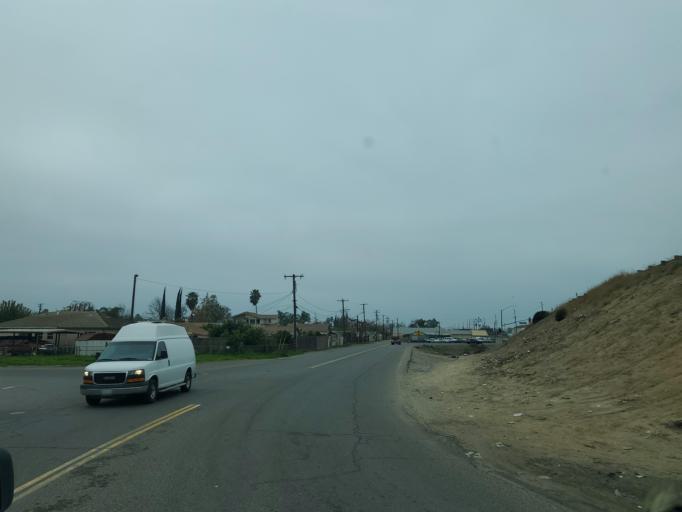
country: US
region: California
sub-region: Stanislaus County
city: Bystrom
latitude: 37.6091
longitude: -120.9781
